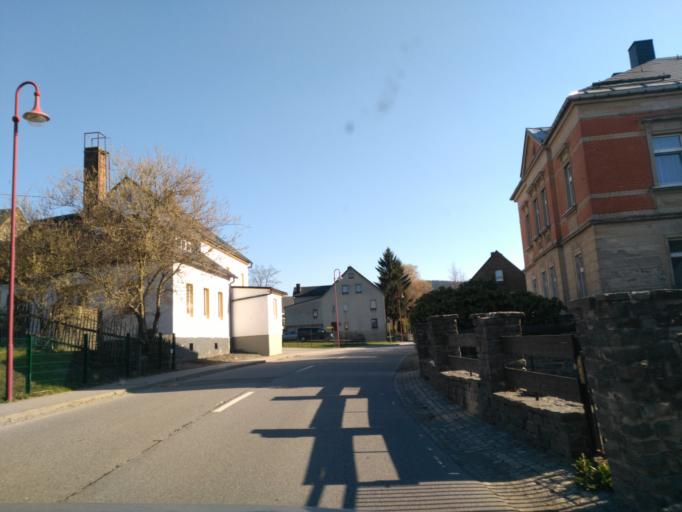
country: DE
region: Saxony
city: Crottendorf
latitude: 50.5049
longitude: 12.9369
